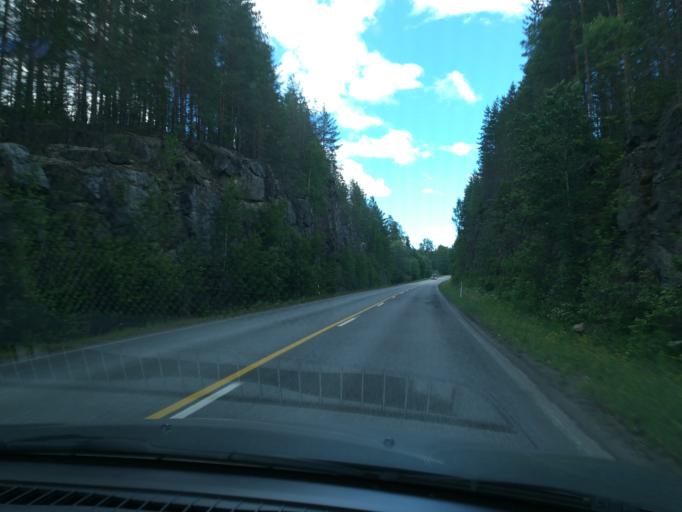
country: FI
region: Southern Savonia
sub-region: Mikkeli
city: Hirvensalmi
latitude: 61.6707
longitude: 26.8787
